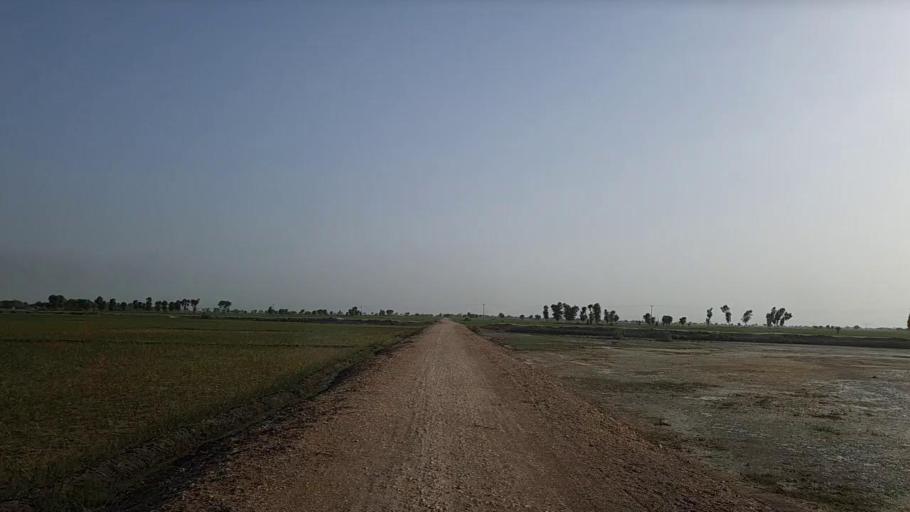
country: PK
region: Sindh
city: Sita Road
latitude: 27.1024
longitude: 67.8870
